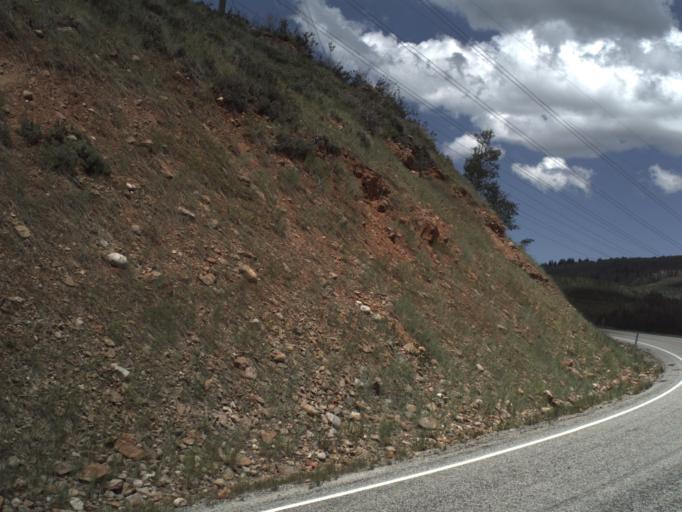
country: US
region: Utah
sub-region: Weber County
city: Wolf Creek
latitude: 41.4026
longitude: -111.5441
